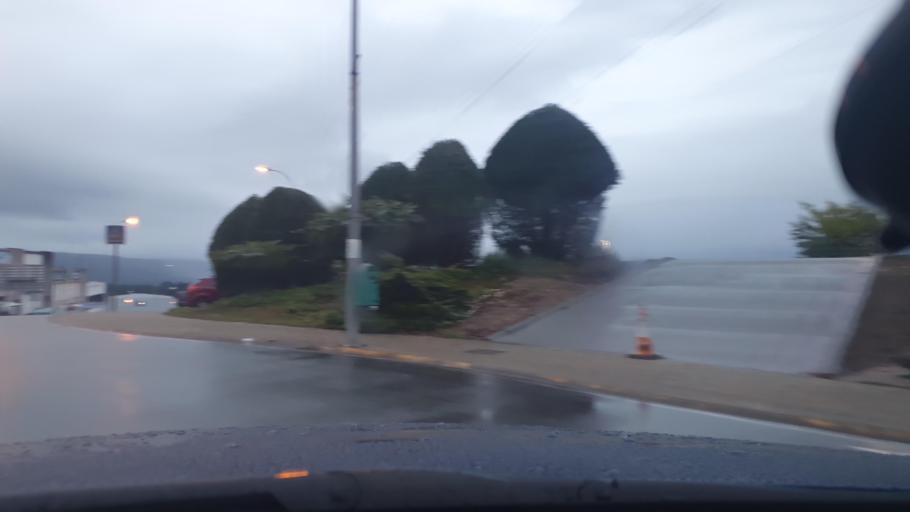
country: ES
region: Galicia
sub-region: Provincia da Coruna
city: Santiago de Compostela
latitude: 42.8525
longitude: -8.5819
